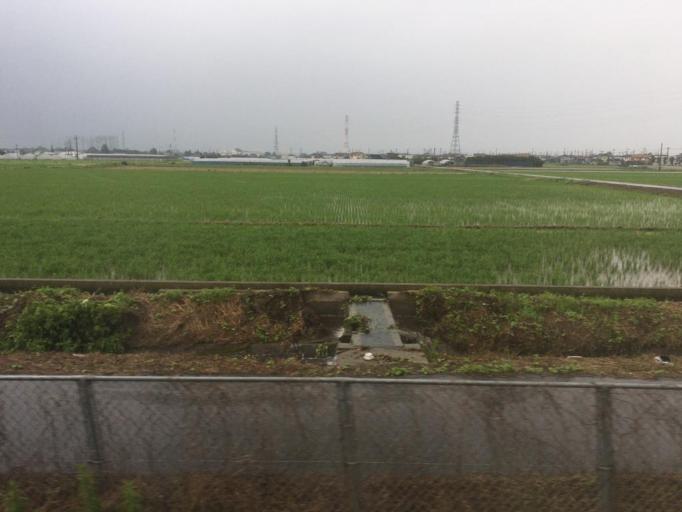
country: JP
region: Tochigi
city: Ashikaga
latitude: 36.3165
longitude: 139.4160
